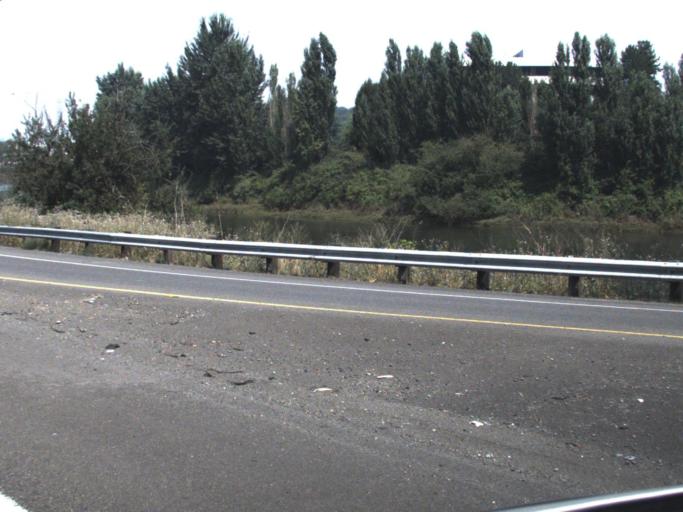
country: US
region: Washington
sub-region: King County
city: Riverton
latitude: 47.5004
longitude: -122.2972
